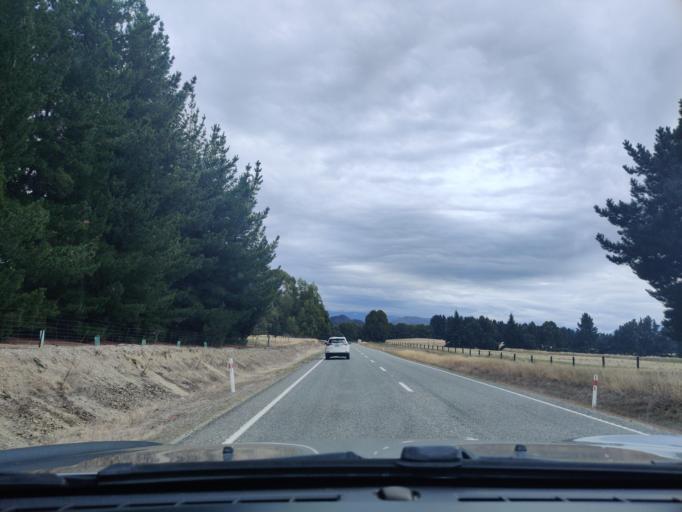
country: NZ
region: Otago
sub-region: Queenstown-Lakes District
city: Wanaka
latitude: -44.7096
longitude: 169.2062
